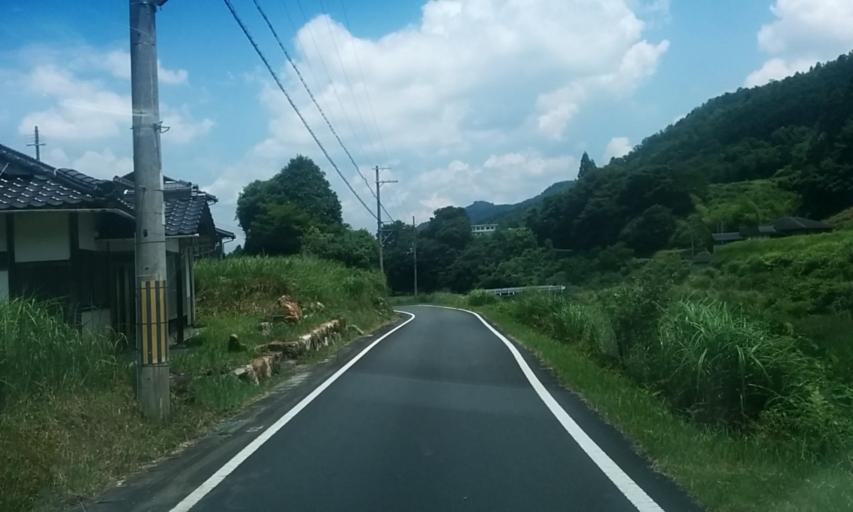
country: JP
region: Kyoto
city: Ayabe
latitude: 35.1908
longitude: 135.2163
